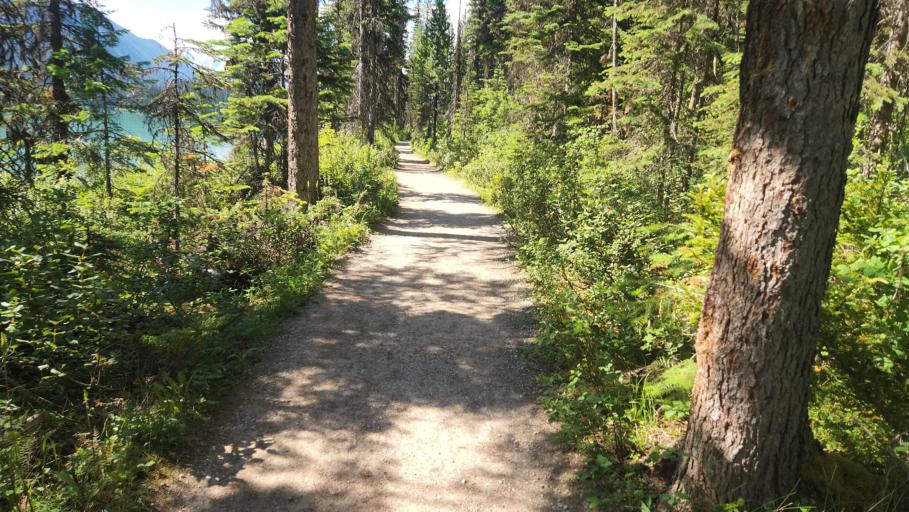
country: CA
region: Alberta
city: Lake Louise
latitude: 51.4477
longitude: -116.5344
